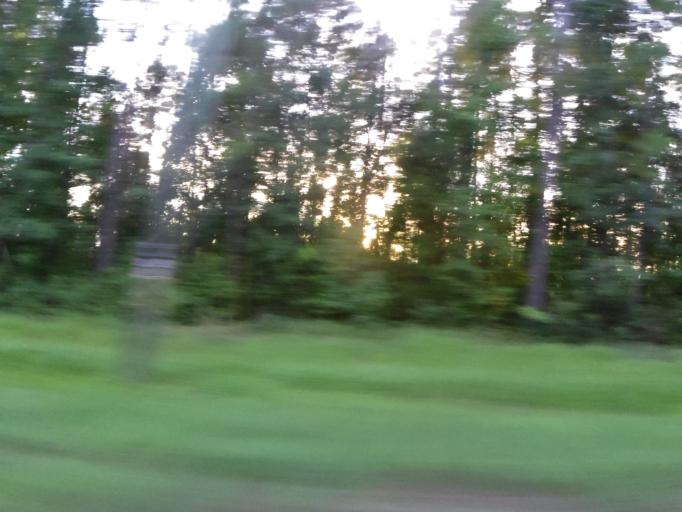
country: US
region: Georgia
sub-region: Camden County
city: Woodbine
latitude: 31.0140
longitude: -81.7315
